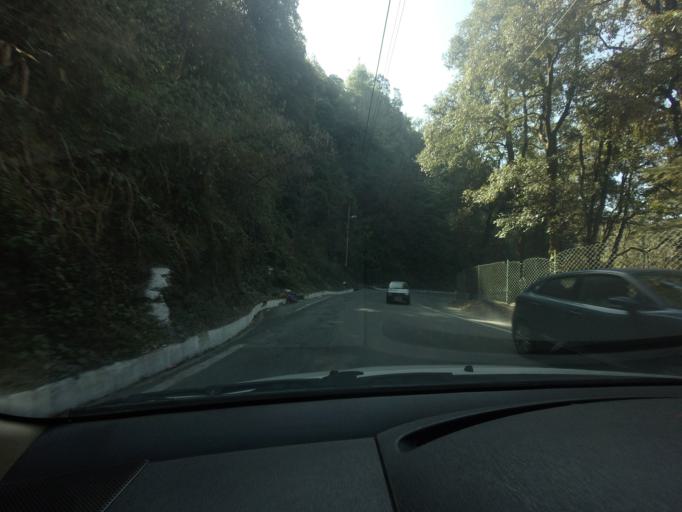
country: IN
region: Himachal Pradesh
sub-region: Shimla
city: Jutogh
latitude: 31.0980
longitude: 77.1341
